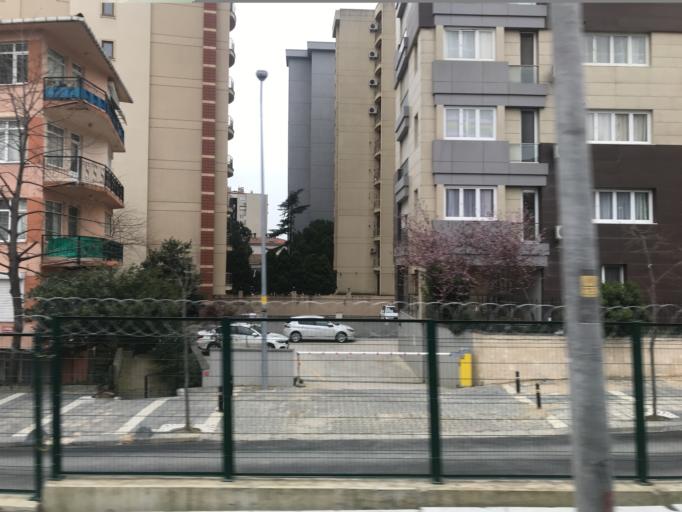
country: TR
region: Istanbul
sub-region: Atasehir
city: Atasehir
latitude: 40.9595
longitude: 29.0890
